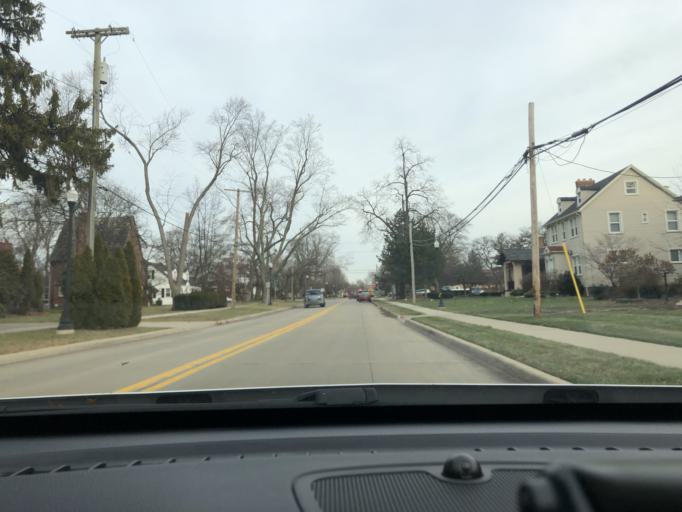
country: US
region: Michigan
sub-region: Wayne County
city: Dearborn Heights
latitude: 42.3049
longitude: -83.2552
